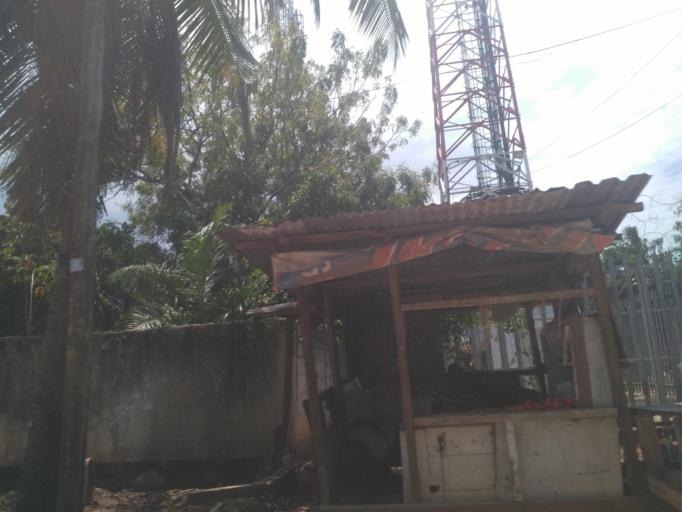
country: TZ
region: Dar es Salaam
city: Magomeni
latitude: -6.7433
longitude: 39.2773
